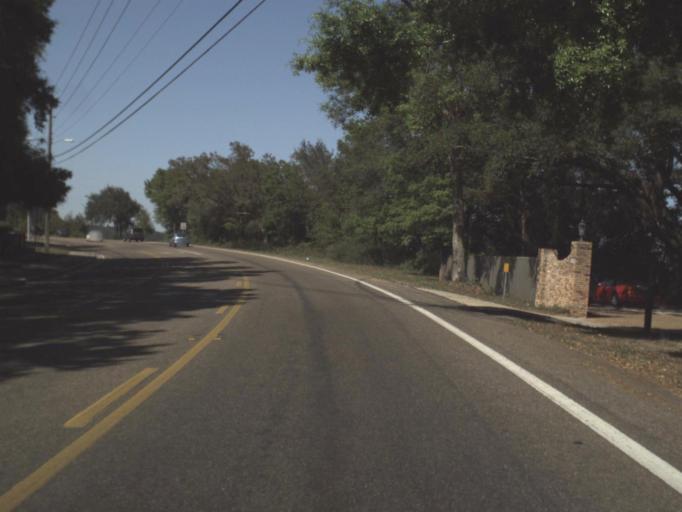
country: US
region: Florida
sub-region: Escambia County
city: East Pensacola Heights
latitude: 30.4349
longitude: -87.1741
